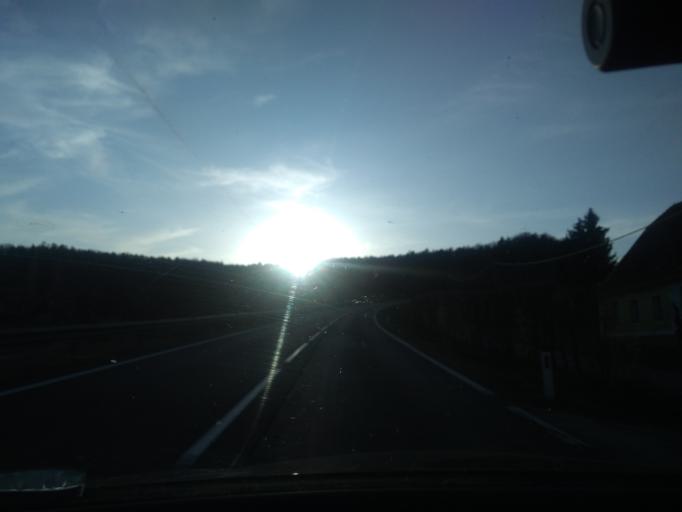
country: AT
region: Styria
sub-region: Politischer Bezirk Graz-Umgebung
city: Hausmannstatten
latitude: 46.9840
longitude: 15.5507
